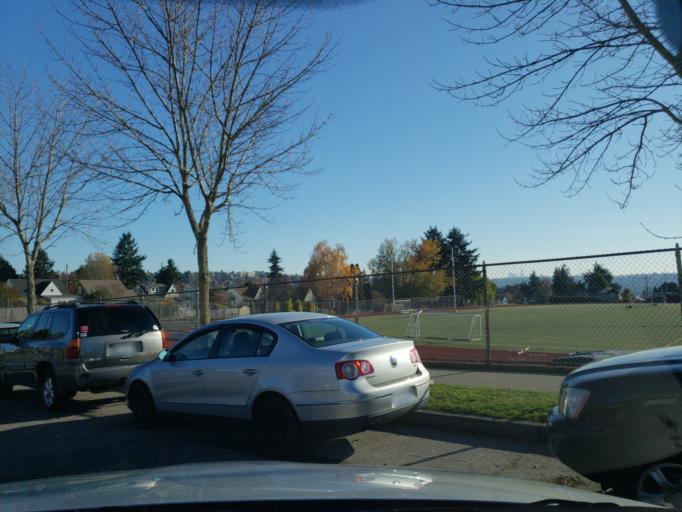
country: US
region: Washington
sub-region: King County
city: Seattle
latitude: 47.6778
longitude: -122.3735
